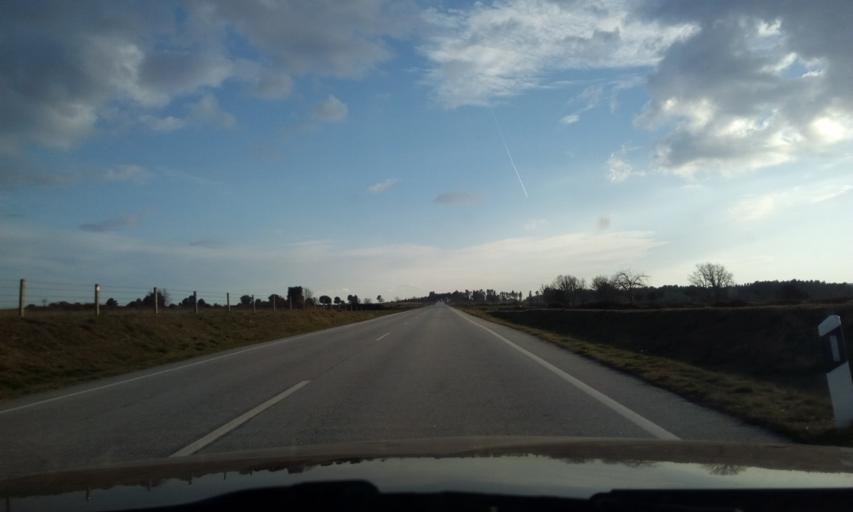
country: PT
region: Guarda
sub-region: Pinhel
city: Pinhel
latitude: 40.6521
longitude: -6.9671
